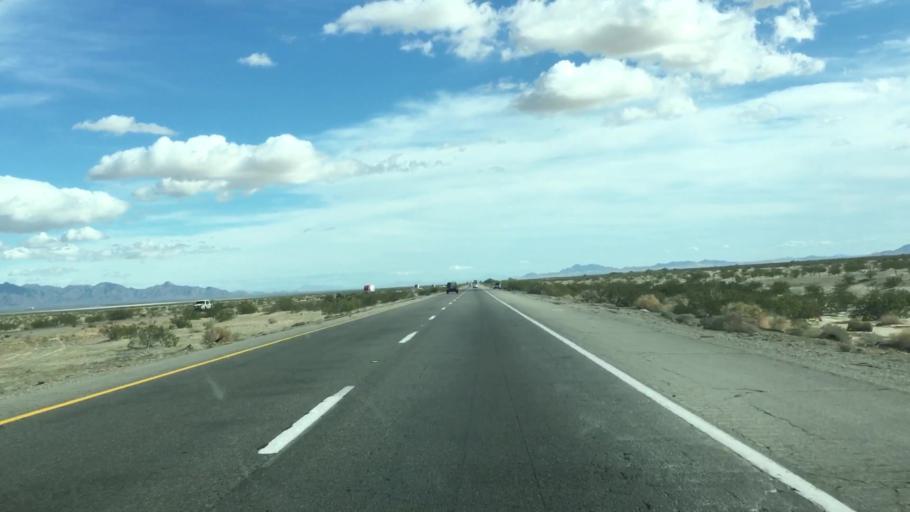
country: US
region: California
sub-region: Riverside County
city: Mesa Verde
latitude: 33.6435
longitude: -115.1118
